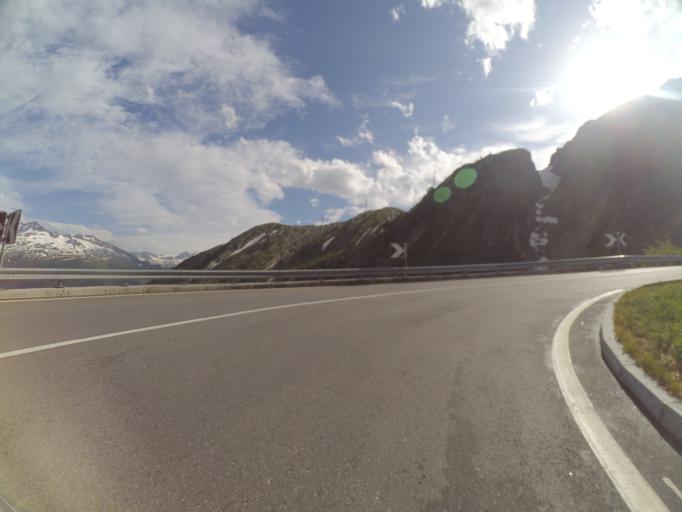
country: IT
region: Piedmont
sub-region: Provincia Verbano-Cusio-Ossola
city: Formazza
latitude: 46.5618
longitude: 8.3515
